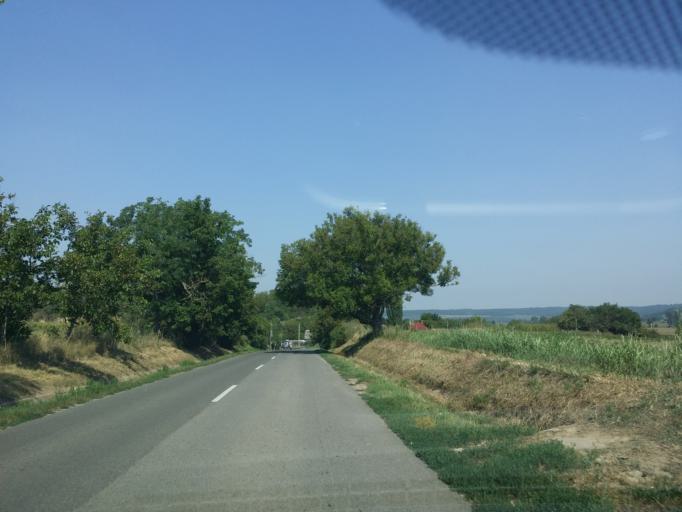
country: HU
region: Tolna
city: Hogyesz
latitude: 46.5708
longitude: 18.3767
